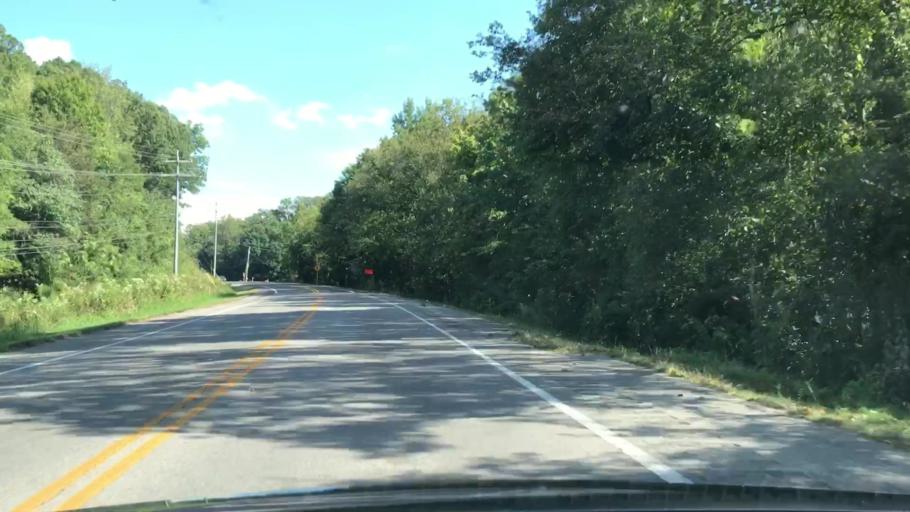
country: US
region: Alabama
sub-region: Limestone County
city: Ardmore
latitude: 35.0061
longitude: -86.8739
